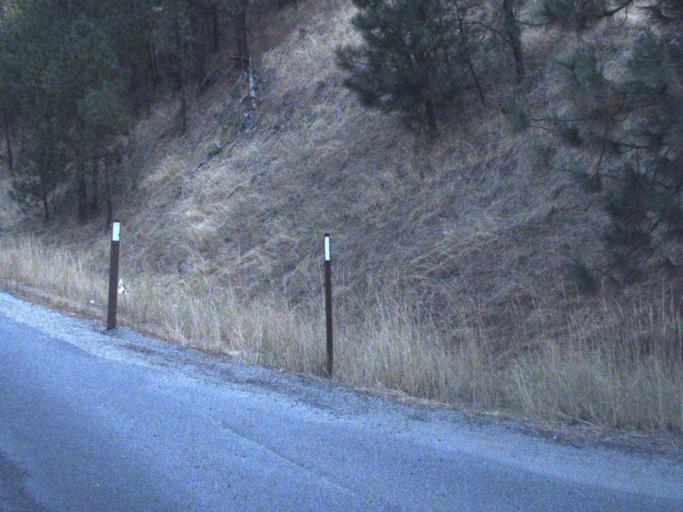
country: US
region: Washington
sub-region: Spokane County
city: Fairwood
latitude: 47.7834
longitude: -117.5297
